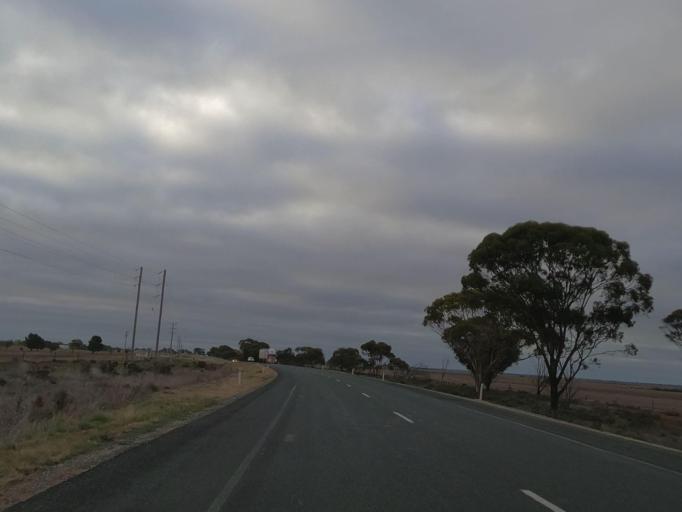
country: AU
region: Victoria
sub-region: Swan Hill
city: Swan Hill
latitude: -35.5848
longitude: 143.7902
